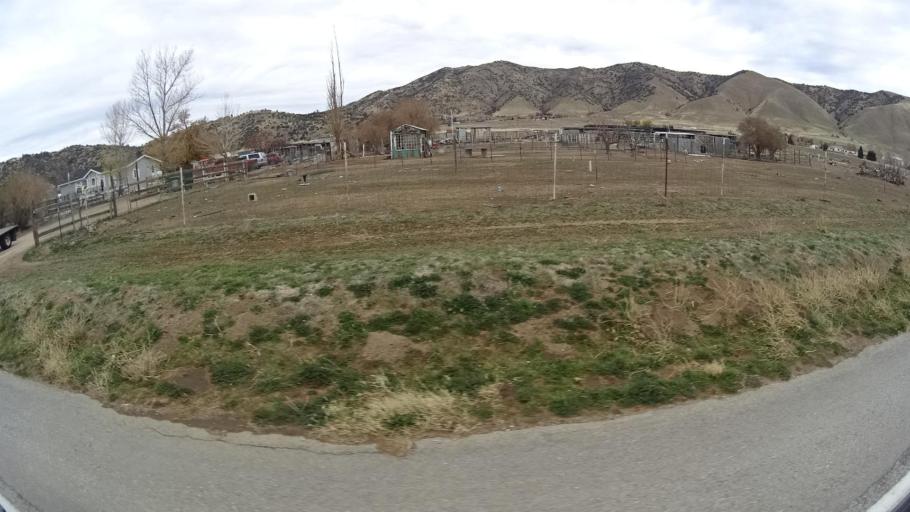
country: US
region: California
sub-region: Kern County
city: Bear Valley Springs
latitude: 35.1279
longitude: -118.5770
